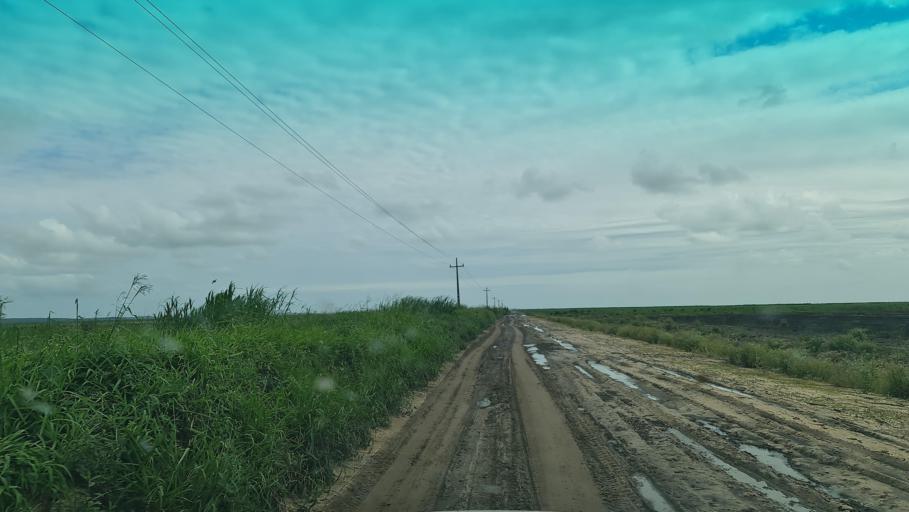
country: MZ
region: Maputo
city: Manhica
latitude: -25.4399
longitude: 32.8405
